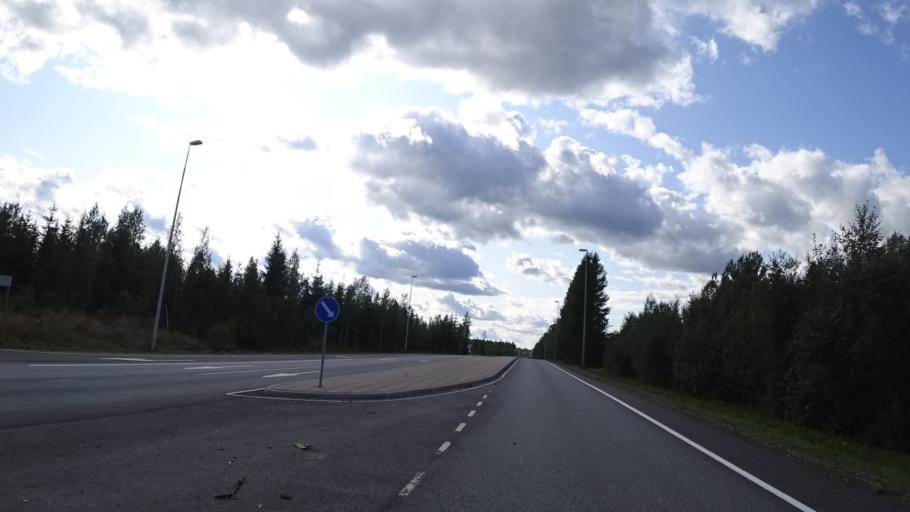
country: RU
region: Republic of Karelia
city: Vyartsilya
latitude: 62.1766
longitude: 30.5796
